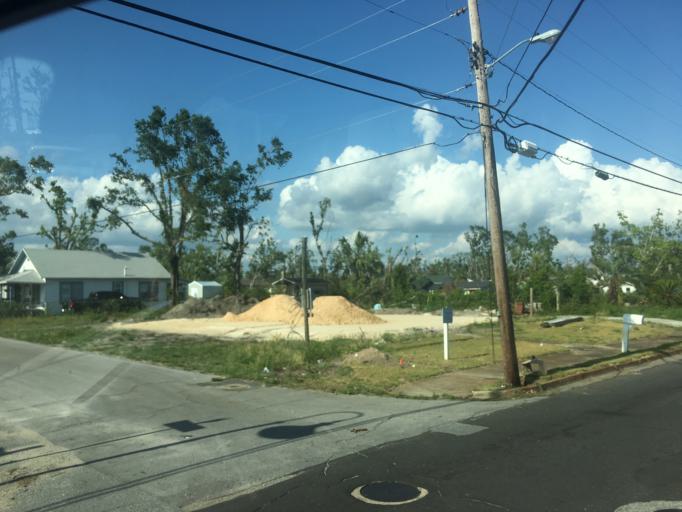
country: US
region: Florida
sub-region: Bay County
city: Cedar Grove
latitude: 30.1531
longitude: -85.6322
